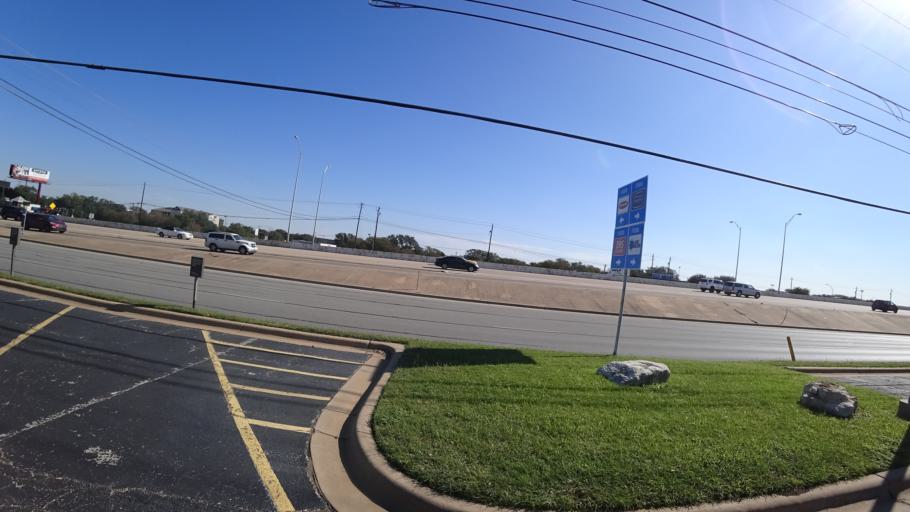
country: US
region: Texas
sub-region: Williamson County
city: Jollyville
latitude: 30.3966
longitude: -97.7469
